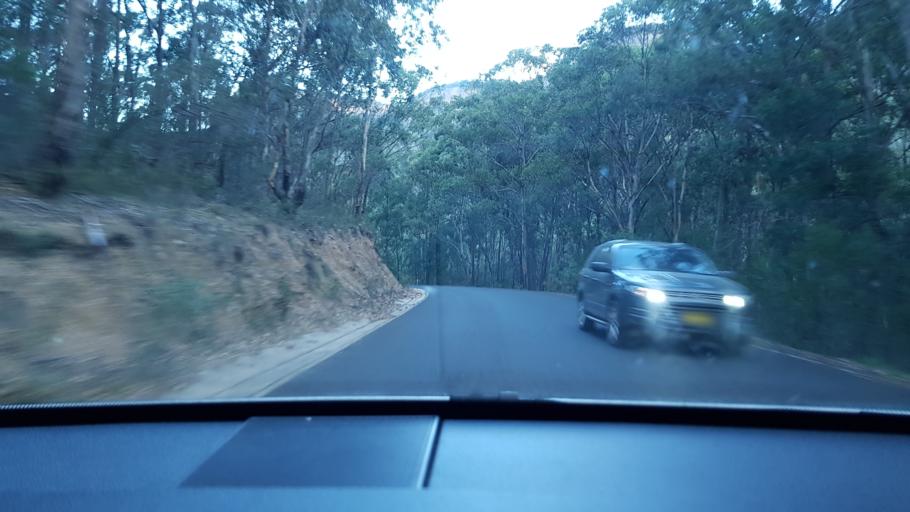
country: AU
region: New South Wales
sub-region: Lithgow
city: Portland
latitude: -33.3053
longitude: 150.1183
